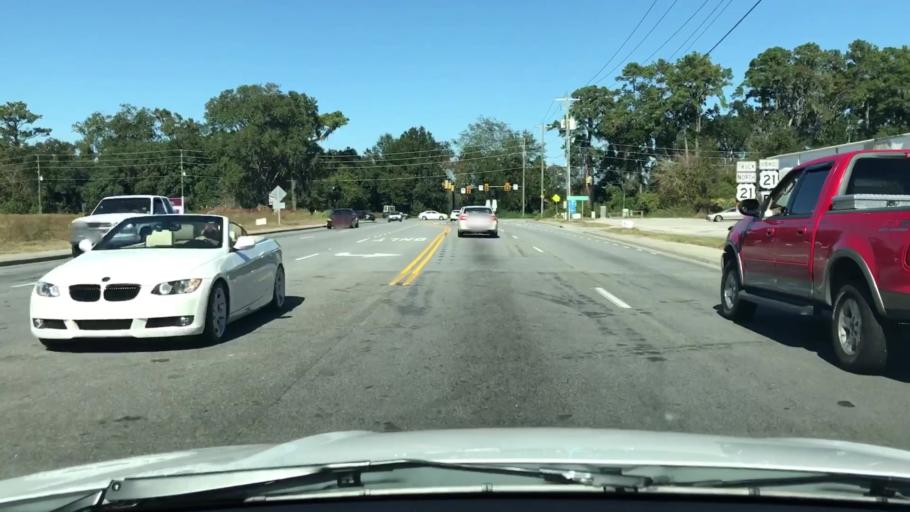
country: US
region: South Carolina
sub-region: Beaufort County
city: Burton
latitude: 32.4405
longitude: -80.7217
